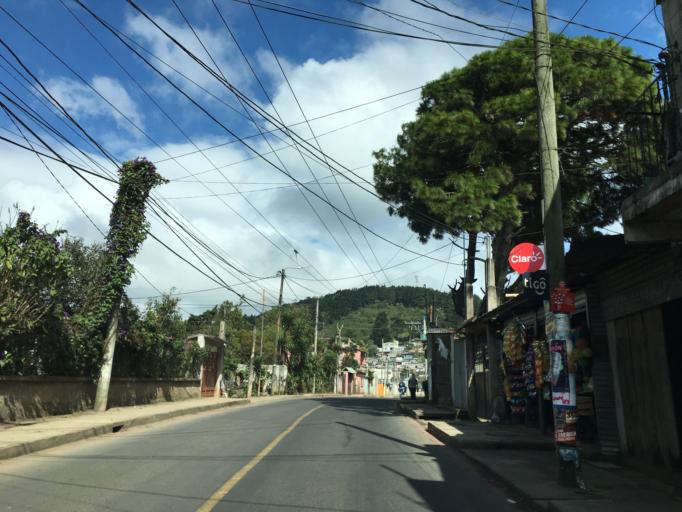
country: GT
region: Guatemala
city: San Jose Pinula
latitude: 14.5472
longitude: -90.4406
